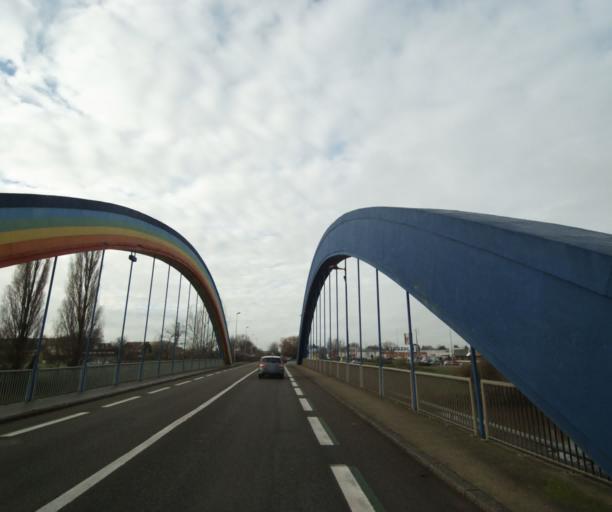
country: FR
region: Pays de la Loire
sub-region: Departement de la Sarthe
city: Allonnes
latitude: 47.9746
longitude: 0.1613
